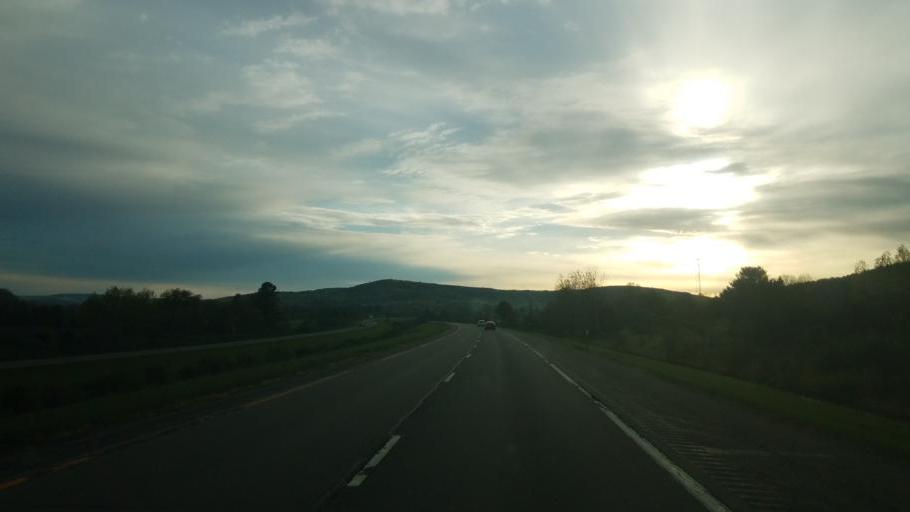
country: US
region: New York
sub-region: Allegany County
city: Belmont
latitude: 42.2948
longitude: -77.9675
